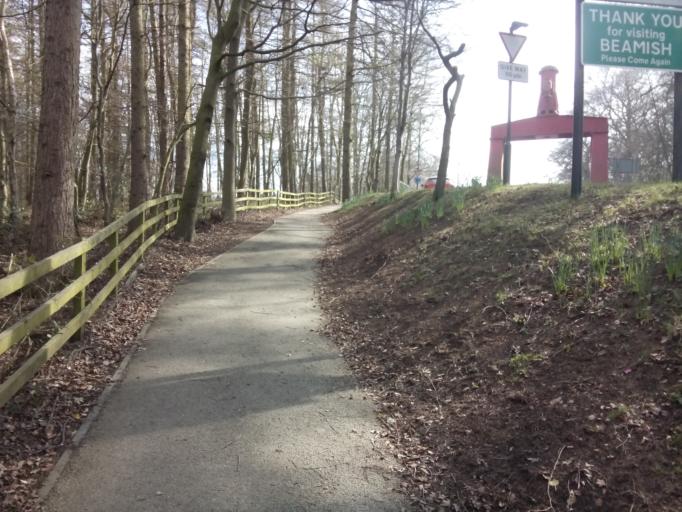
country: GB
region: England
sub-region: County Durham
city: Stanley
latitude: 54.8798
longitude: -1.6585
